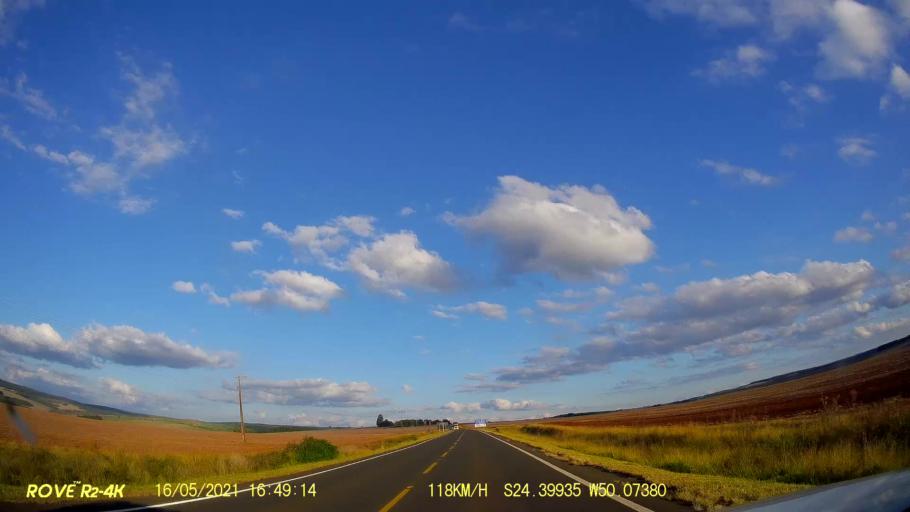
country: BR
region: Parana
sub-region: Pirai Do Sul
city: Pirai do Sul
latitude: -24.3995
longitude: -50.0738
